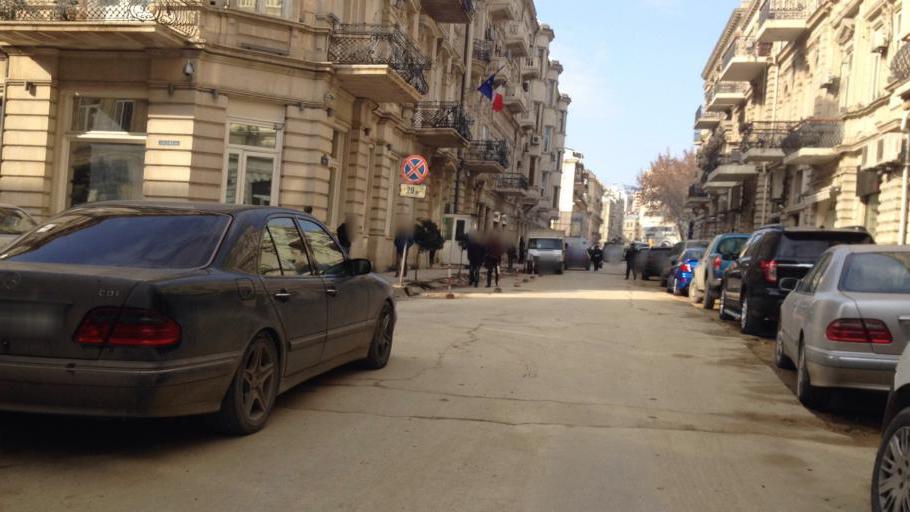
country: AZ
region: Baki
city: Badamdar
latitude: 40.3703
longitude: 49.8409
